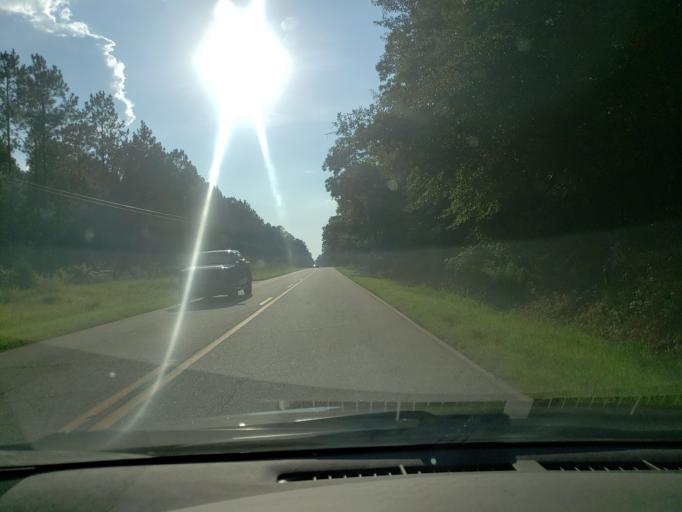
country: US
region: Georgia
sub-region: Dougherty County
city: Albany
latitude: 31.5758
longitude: -84.3506
